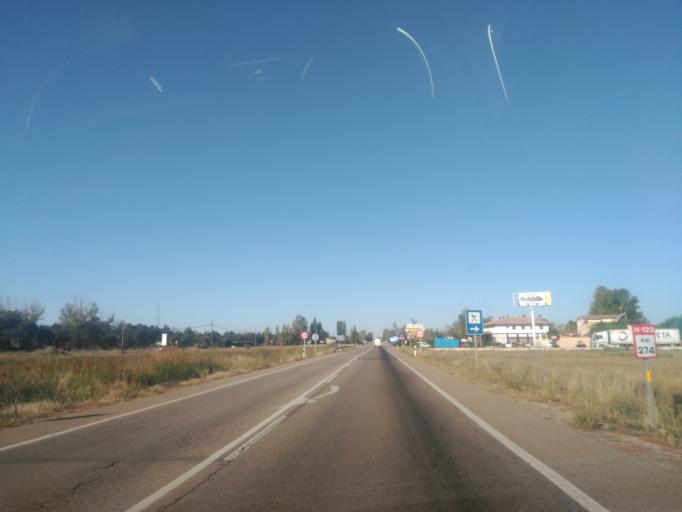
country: ES
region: Castille and Leon
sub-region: Provincia de Burgos
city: Villalba de Duero
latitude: 41.6631
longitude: -3.7400
